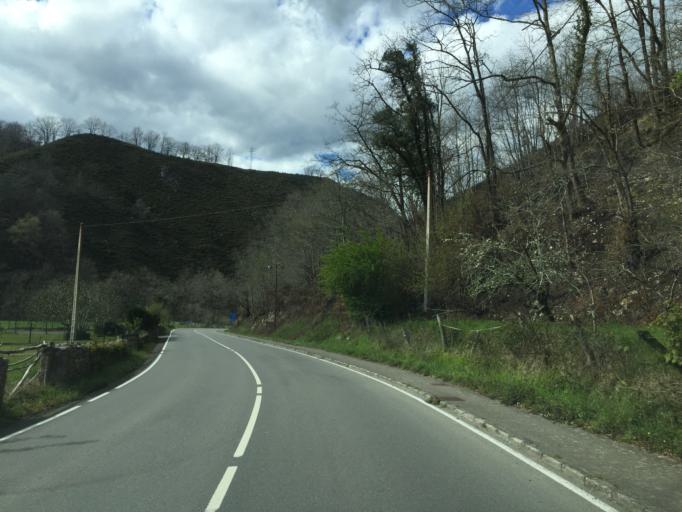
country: ES
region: Asturias
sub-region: Province of Asturias
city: Cangas de Onis
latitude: 43.3278
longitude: -5.0797
